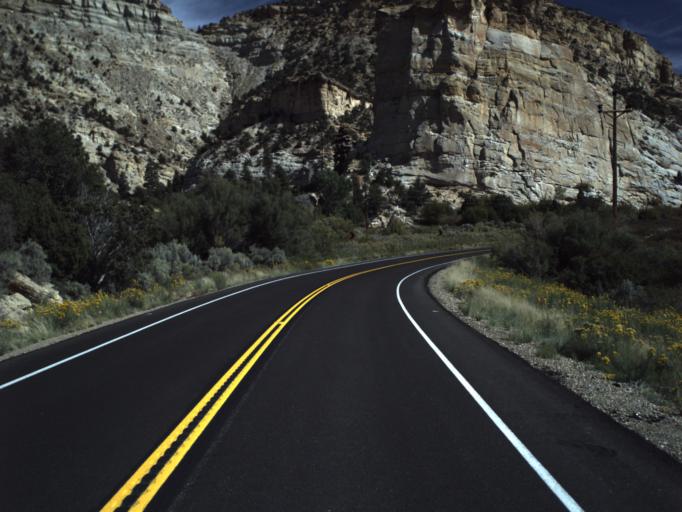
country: US
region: Utah
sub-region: Garfield County
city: Panguitch
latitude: 37.6021
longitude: -111.9168
